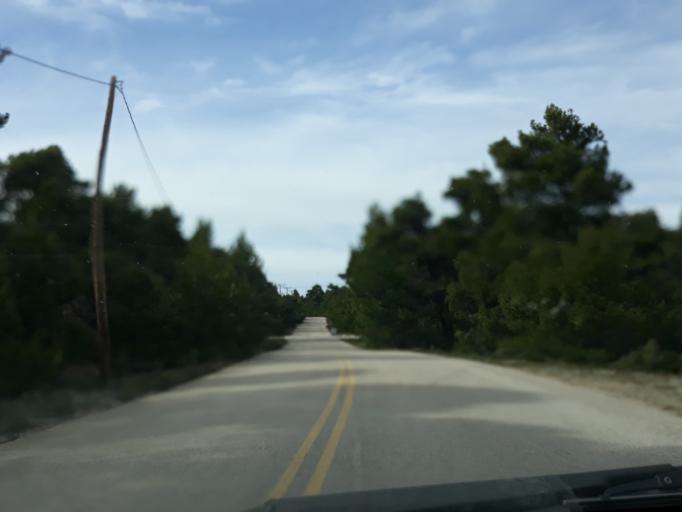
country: GR
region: Attica
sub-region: Nomarchia Anatolikis Attikis
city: Afidnes
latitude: 38.2124
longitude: 23.7976
